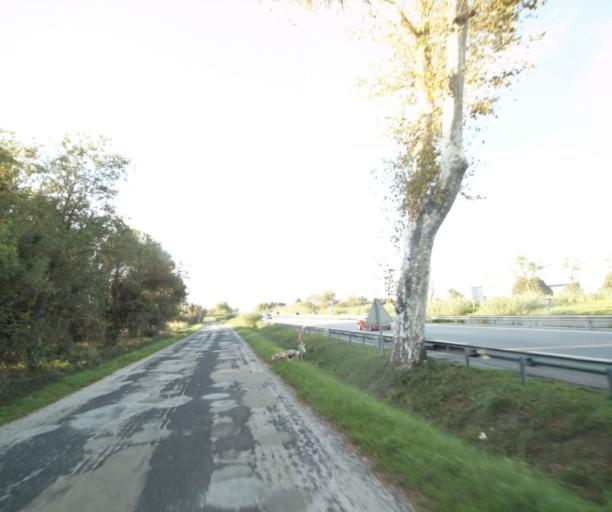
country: FR
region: Languedoc-Roussillon
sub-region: Departement des Pyrenees-Orientales
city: Elne
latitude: 42.5817
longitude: 2.9885
